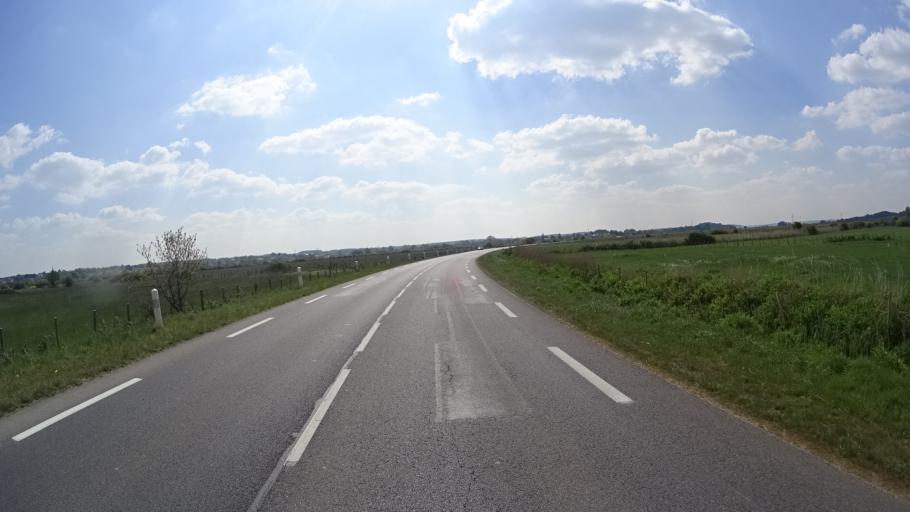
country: FR
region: Brittany
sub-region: Departement du Morbihan
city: Rieux
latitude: 47.5845
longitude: -2.1115
